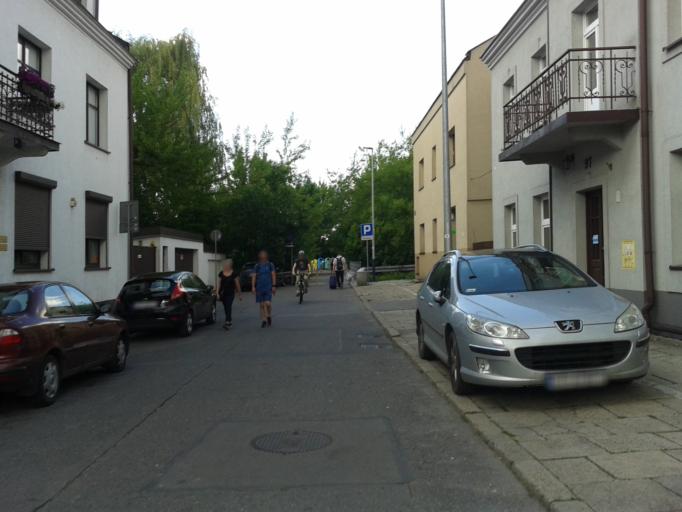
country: PL
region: Lesser Poland Voivodeship
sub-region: Krakow
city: Krakow
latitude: 50.0782
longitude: 19.9599
